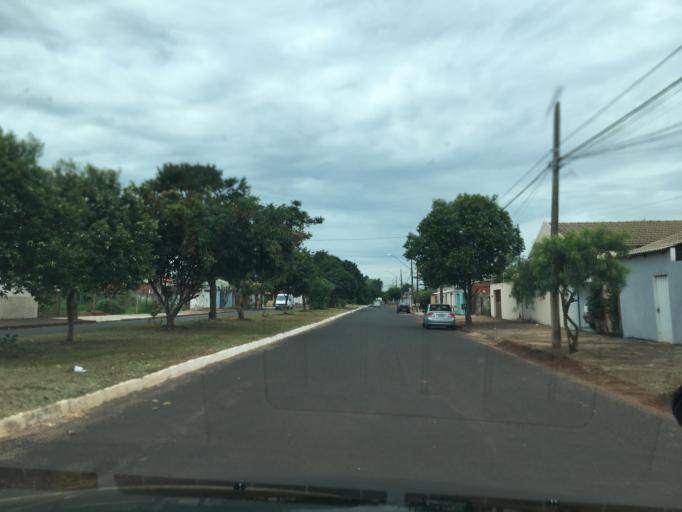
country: BR
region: Minas Gerais
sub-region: Uberlandia
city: Uberlandia
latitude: -18.8795
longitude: -48.2278
